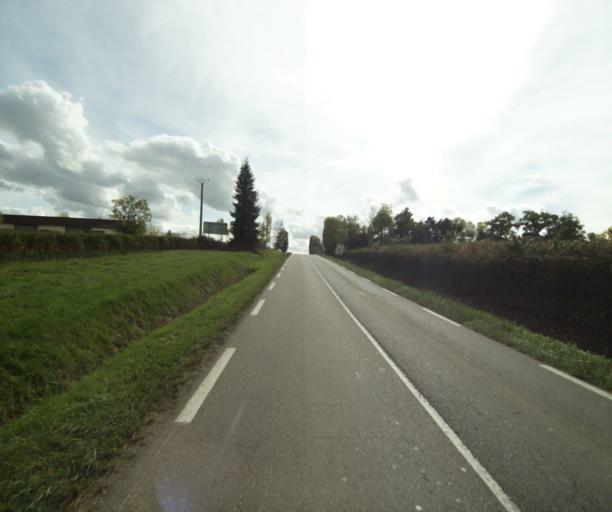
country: FR
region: Midi-Pyrenees
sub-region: Departement du Gers
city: Eauze
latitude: 43.8434
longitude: 0.0929
